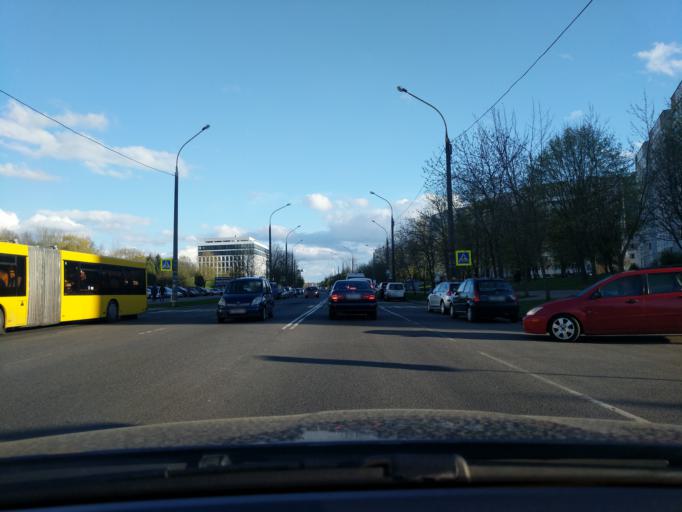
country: BY
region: Minsk
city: Novoye Medvezhino
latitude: 53.9121
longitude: 27.4509
